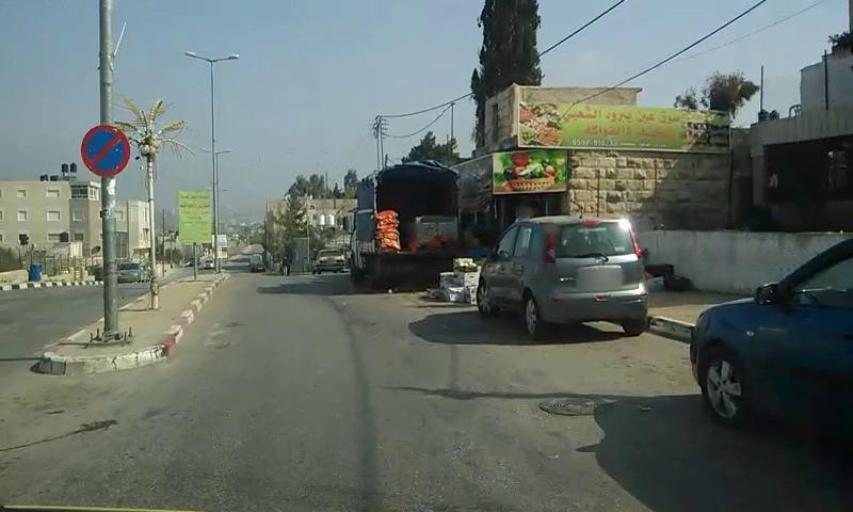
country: PS
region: West Bank
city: `Ayn Yabrud
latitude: 31.9537
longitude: 35.2522
